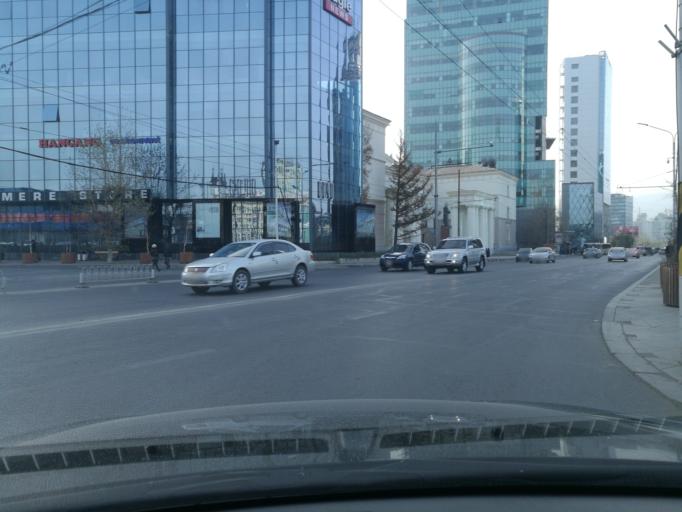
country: MN
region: Ulaanbaatar
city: Ulaanbaatar
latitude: 47.9157
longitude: 106.9158
